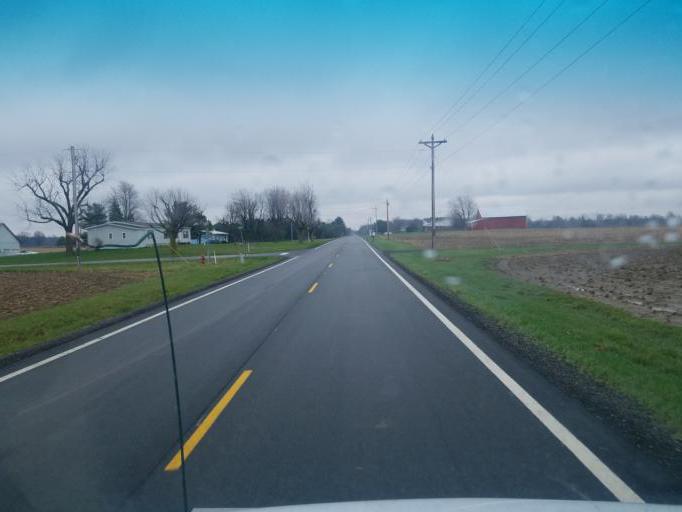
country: US
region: Ohio
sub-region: Huron County
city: Willard
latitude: 40.9602
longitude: -82.8170
